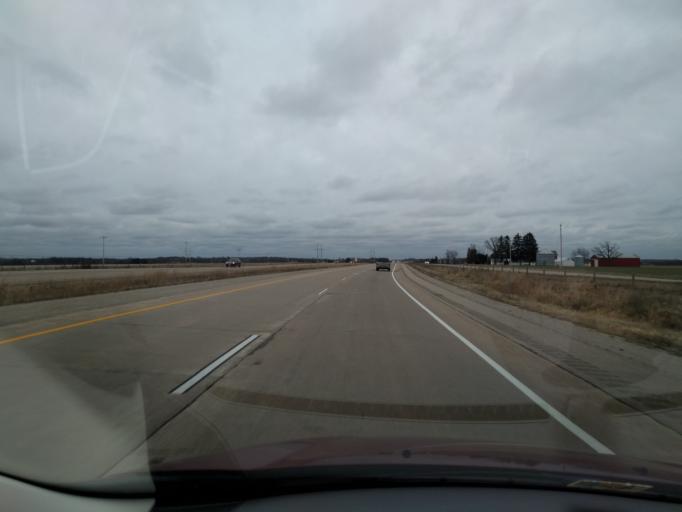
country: US
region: Wisconsin
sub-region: Winnebago County
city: Winneconne
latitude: 44.1797
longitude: -88.6647
